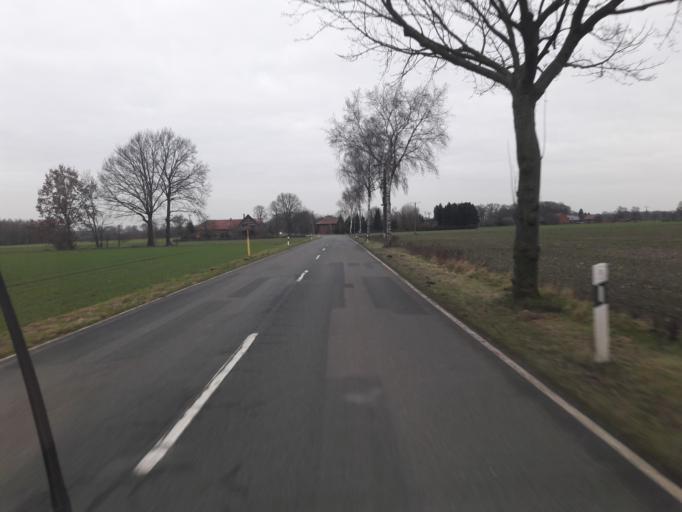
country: DE
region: Lower Saxony
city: Warmsen
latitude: 52.4372
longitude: 8.8596
